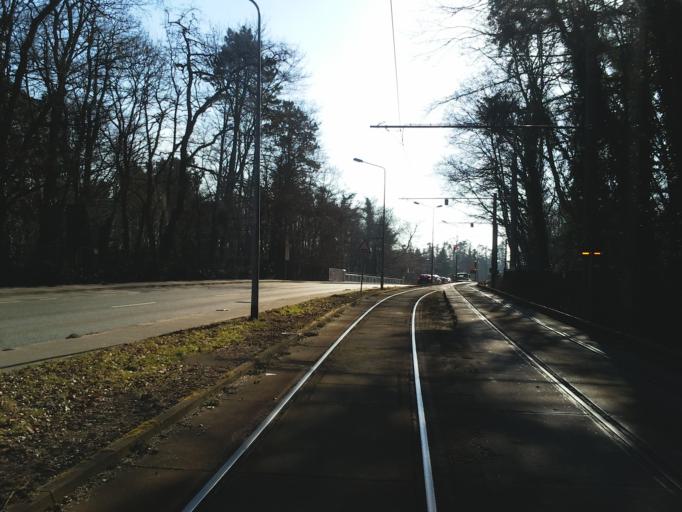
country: DE
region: Mecklenburg-Vorpommern
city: Kritzmow
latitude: 54.0770
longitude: 12.0875
